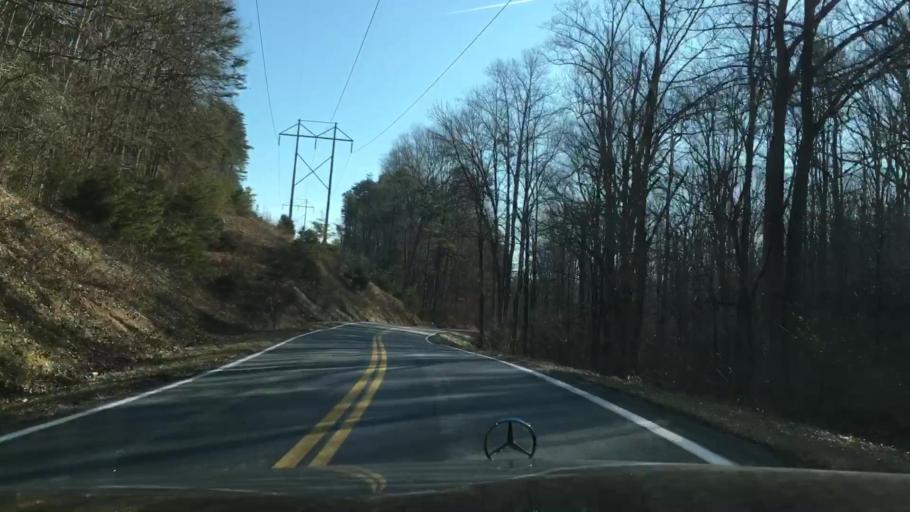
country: US
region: Virginia
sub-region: Campbell County
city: Altavista
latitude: 37.1440
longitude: -79.3305
